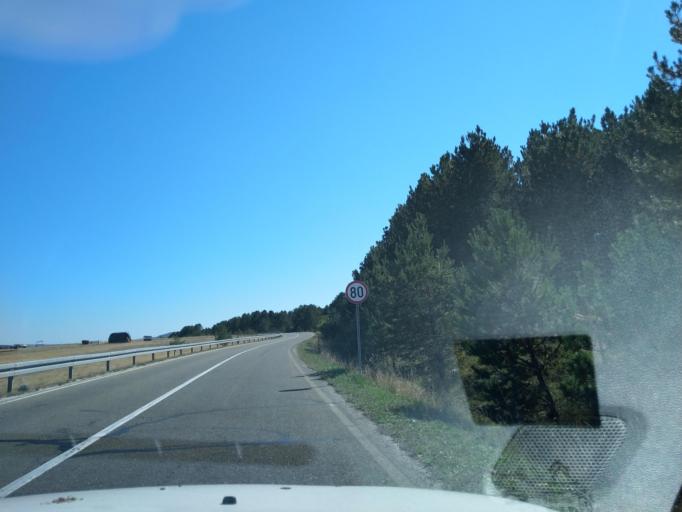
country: RS
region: Central Serbia
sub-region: Zlatiborski Okrug
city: Sjenica
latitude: 43.2644
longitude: 20.0436
